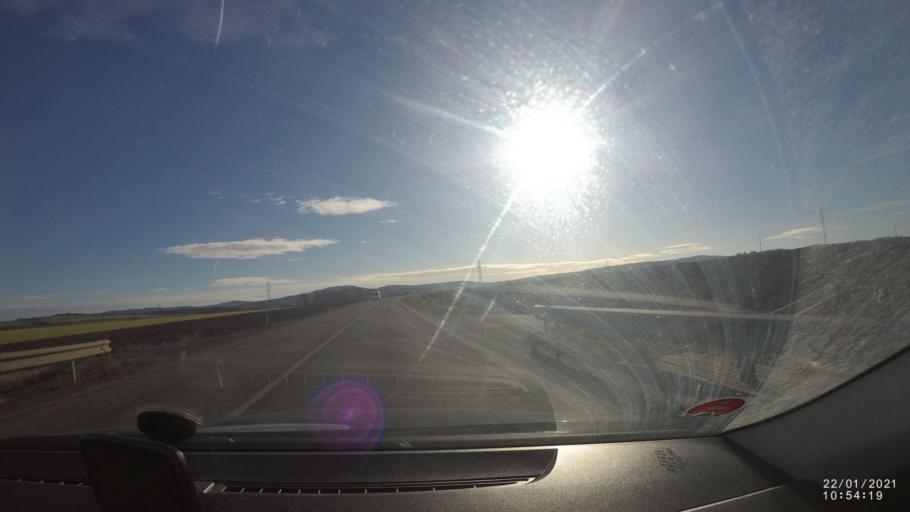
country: CZ
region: Central Bohemia
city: Zebrak
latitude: 49.8595
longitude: 13.9024
